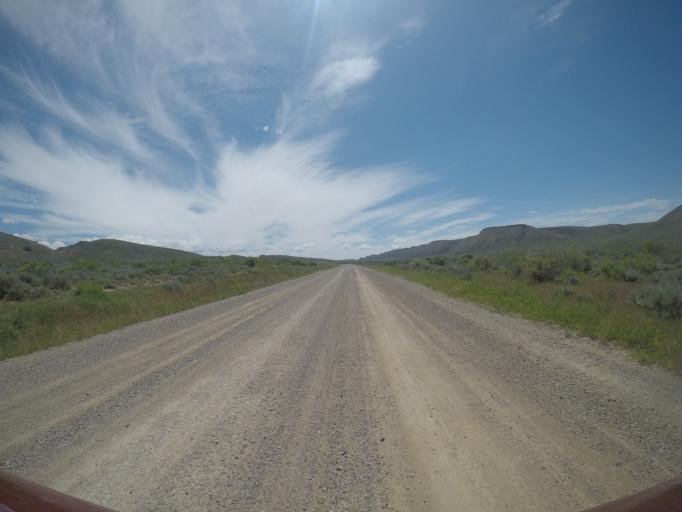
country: US
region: Montana
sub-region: Carbon County
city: Red Lodge
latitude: 45.2068
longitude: -108.8270
